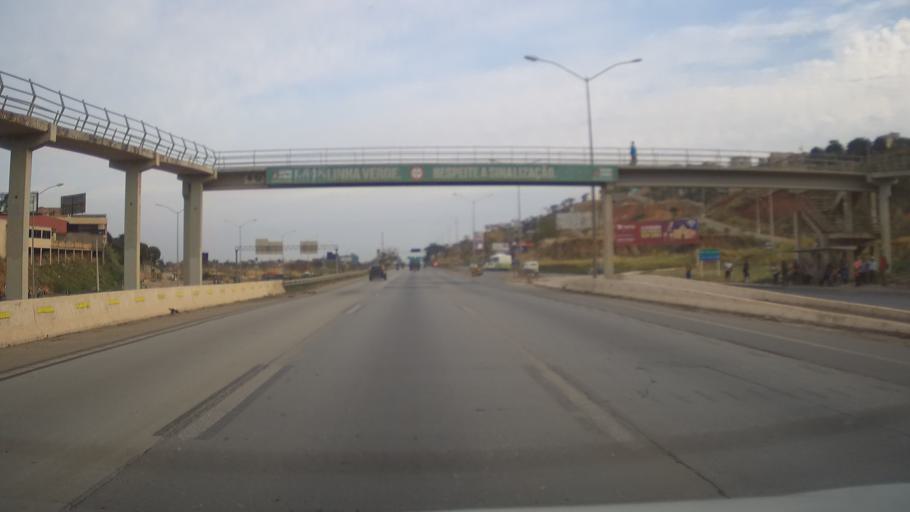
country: BR
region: Minas Gerais
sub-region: Vespasiano
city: Vespasiano
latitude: -19.7723
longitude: -43.9485
